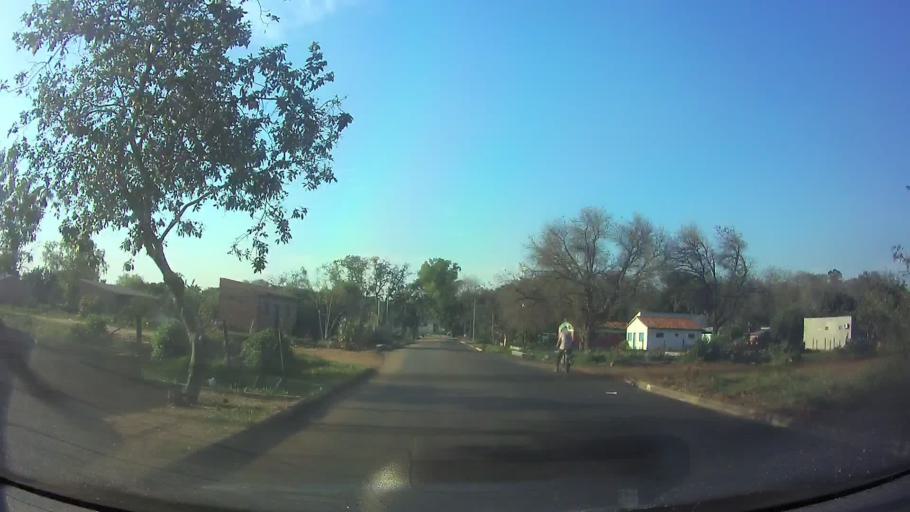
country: PY
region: Central
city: San Lorenzo
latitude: -25.2566
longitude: -57.4799
